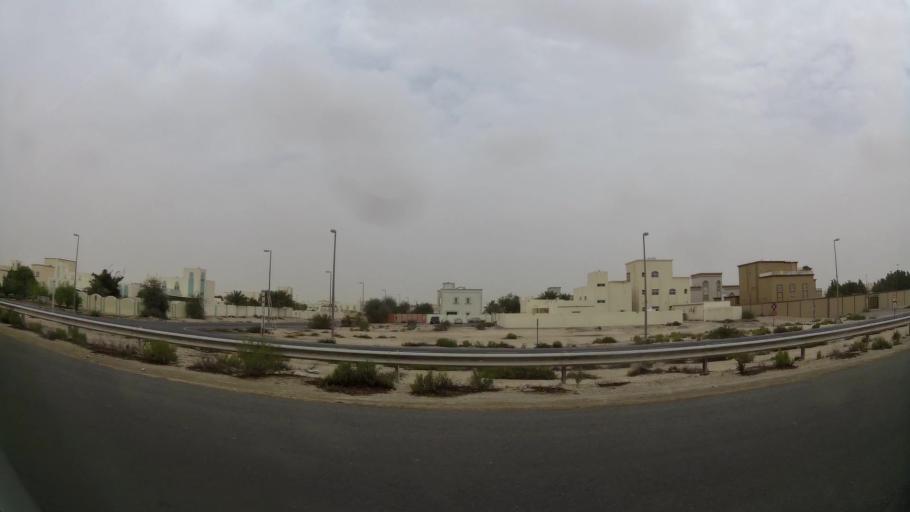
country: AE
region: Abu Dhabi
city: Abu Dhabi
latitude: 24.3930
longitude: 54.7304
